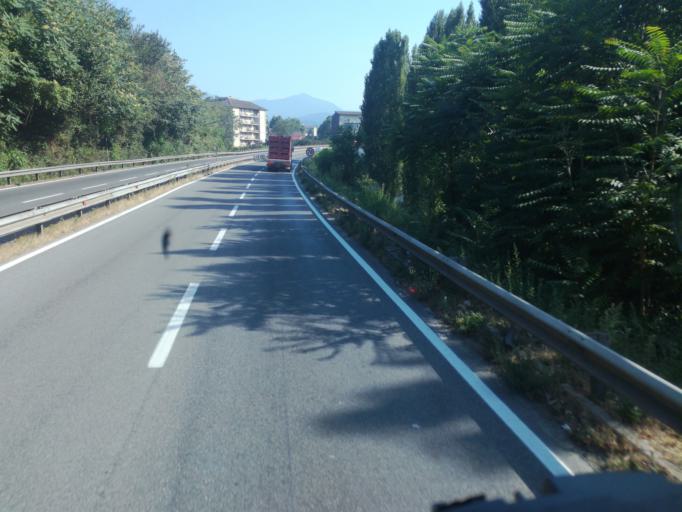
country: IT
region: Campania
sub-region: Provincia di Avellino
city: Atripalda
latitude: 40.9210
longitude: 14.8260
